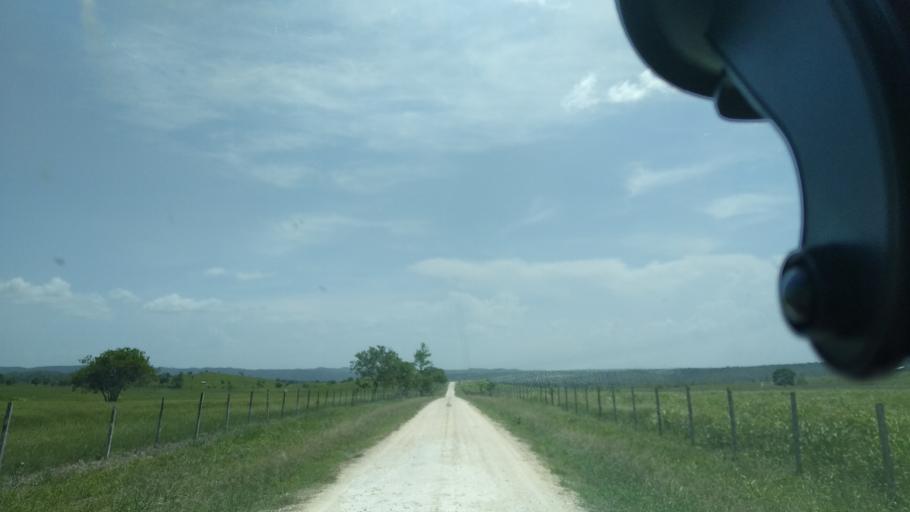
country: BZ
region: Cayo
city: San Ignacio
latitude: 17.2930
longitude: -89.0704
